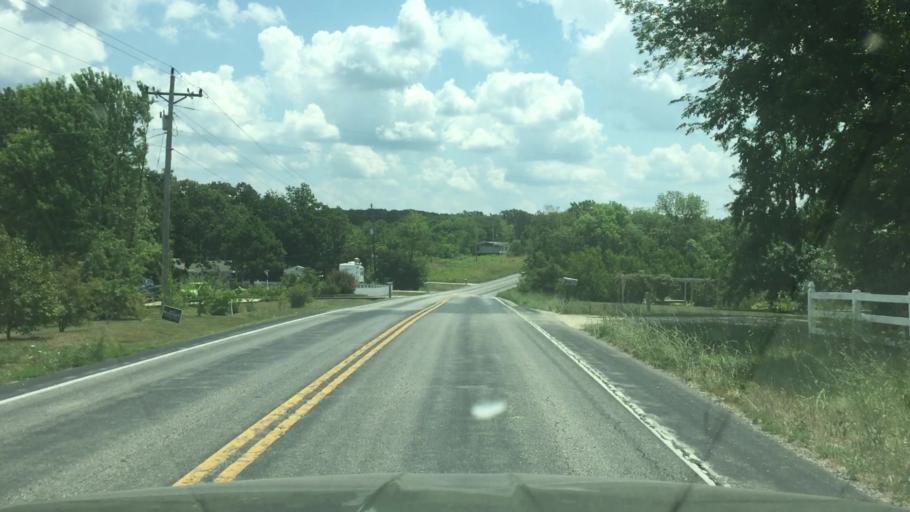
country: US
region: Missouri
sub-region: Miller County
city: Tuscumbia
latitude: 38.1164
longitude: -92.5115
